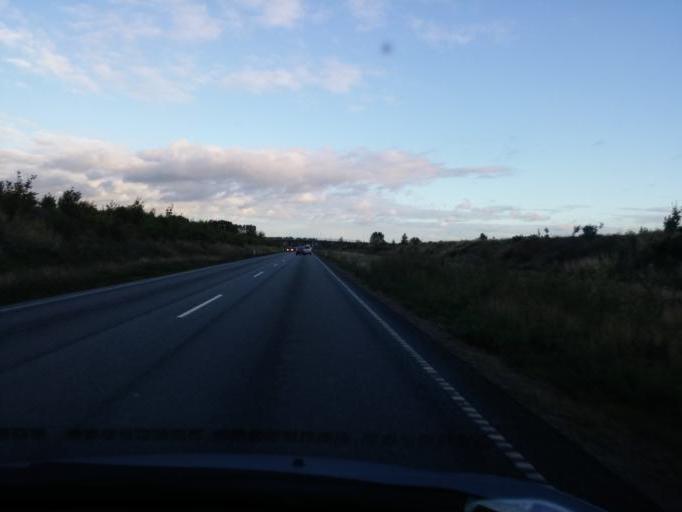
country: DK
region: South Denmark
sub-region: Odense Kommune
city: Bullerup
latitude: 55.4220
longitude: 10.4646
